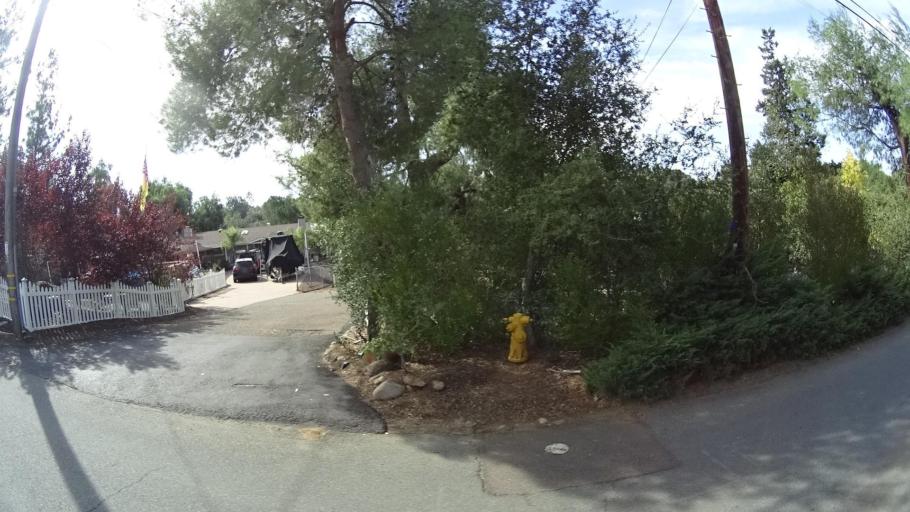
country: US
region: California
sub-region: San Diego County
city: Alpine
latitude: 32.8367
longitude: -116.7854
